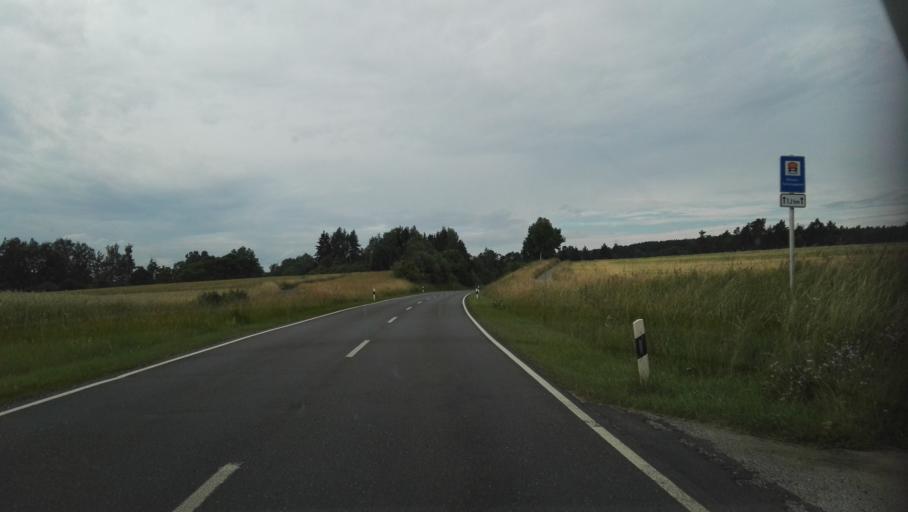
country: DE
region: Bavaria
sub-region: Upper Franconia
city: Hollfeld
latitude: 49.9217
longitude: 11.3062
